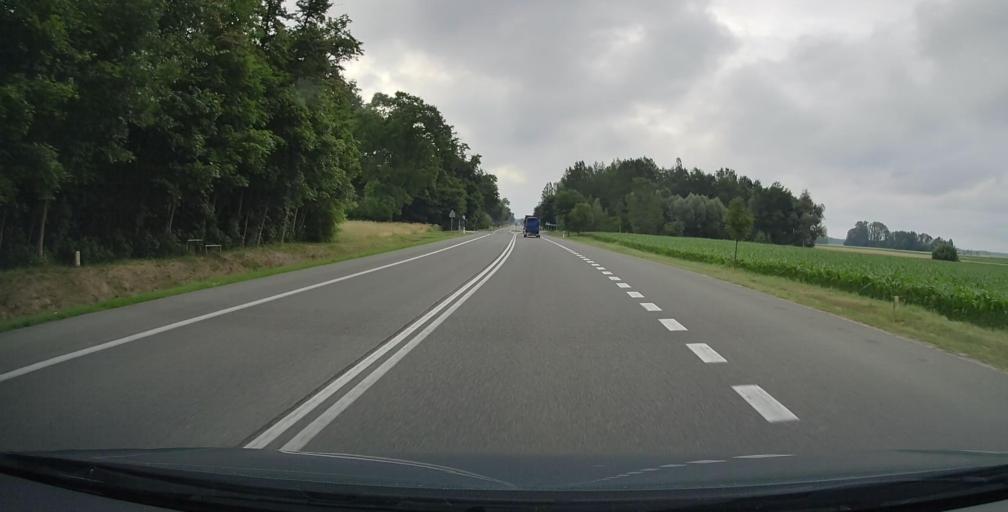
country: PL
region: Lublin Voivodeship
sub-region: Powiat lukowski
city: Trzebieszow
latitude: 52.0570
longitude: 22.5892
